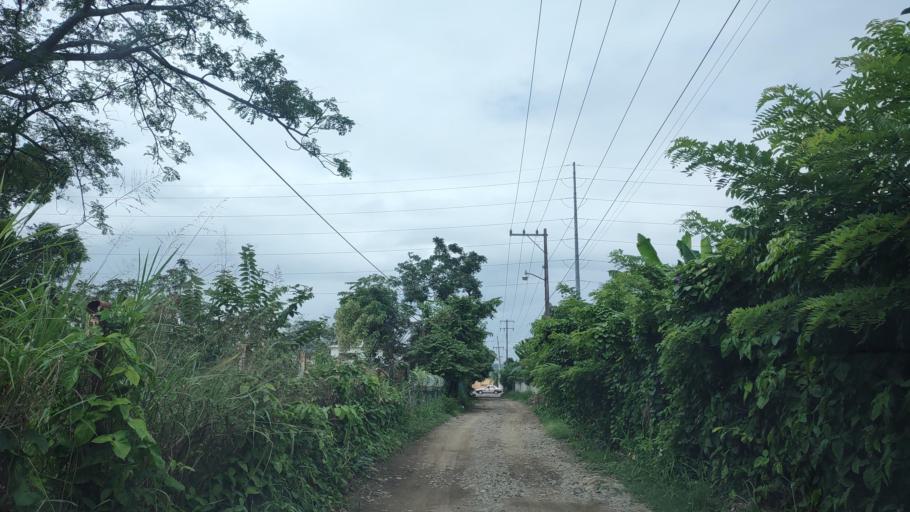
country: MX
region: Veracruz
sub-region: Papantla
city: Residencial Tajin
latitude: 20.5921
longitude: -97.4213
